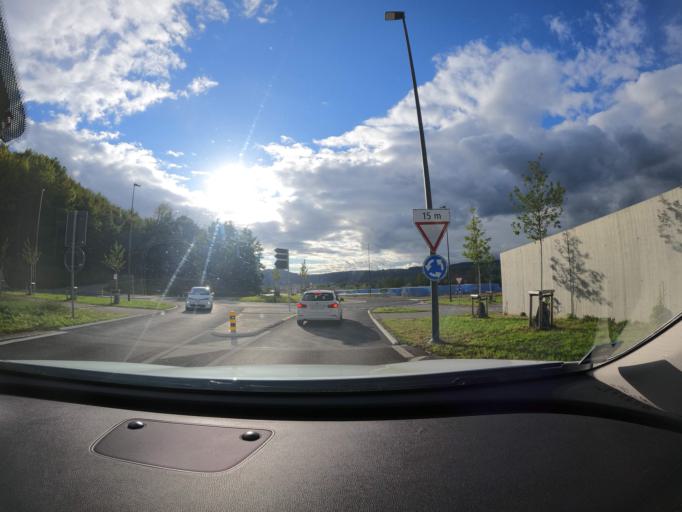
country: CH
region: Aargau
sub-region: Bezirk Brugg
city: Brugg
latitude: 47.4733
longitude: 8.2056
